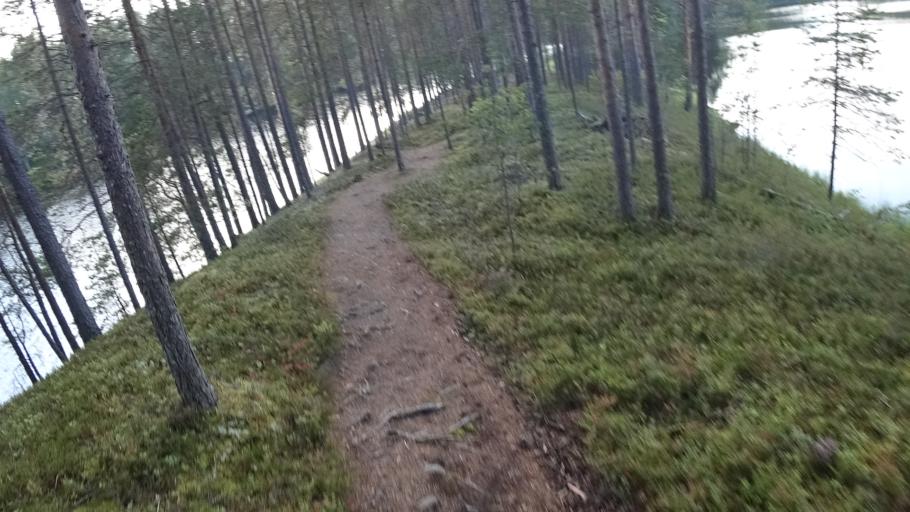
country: FI
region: North Karelia
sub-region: Joensuu
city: Ilomantsi
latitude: 62.5789
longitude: 31.1614
